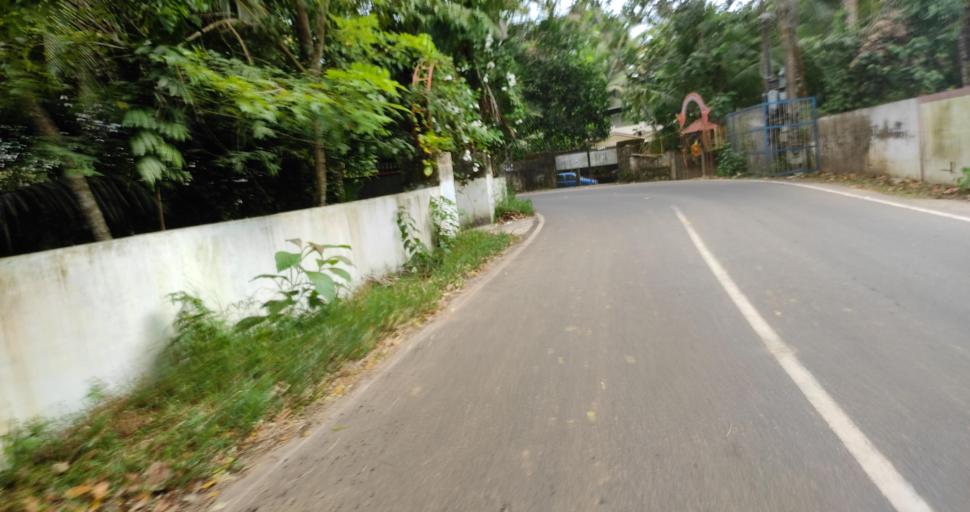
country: IN
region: Kerala
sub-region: Alappuzha
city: Vayalar
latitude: 9.6542
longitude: 76.3129
